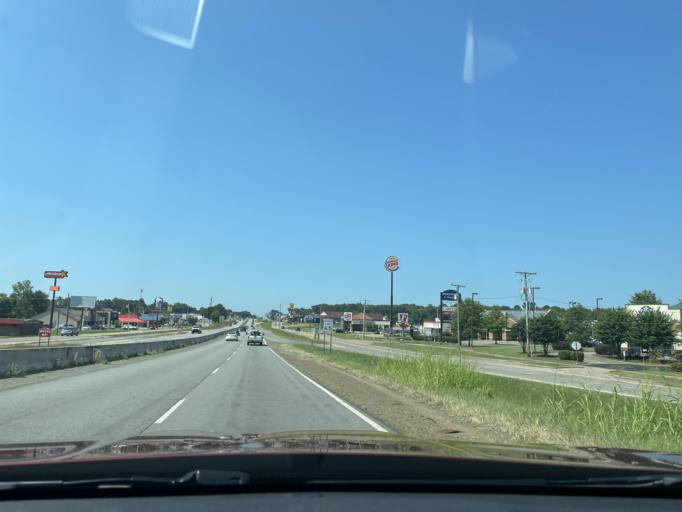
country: US
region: Arkansas
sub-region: Pulaski County
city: Jacksonville
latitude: 34.8861
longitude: -92.1080
